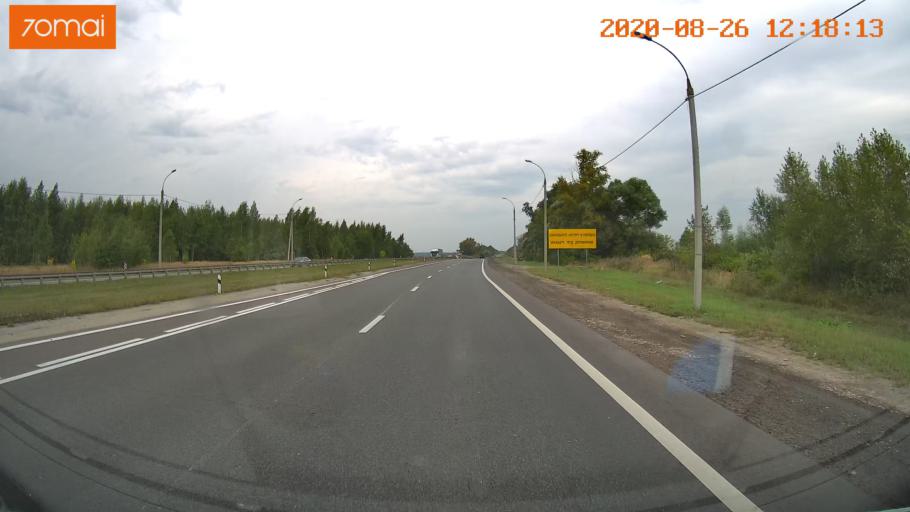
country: RU
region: Rjazan
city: Murmino
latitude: 54.4708
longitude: 40.0216
